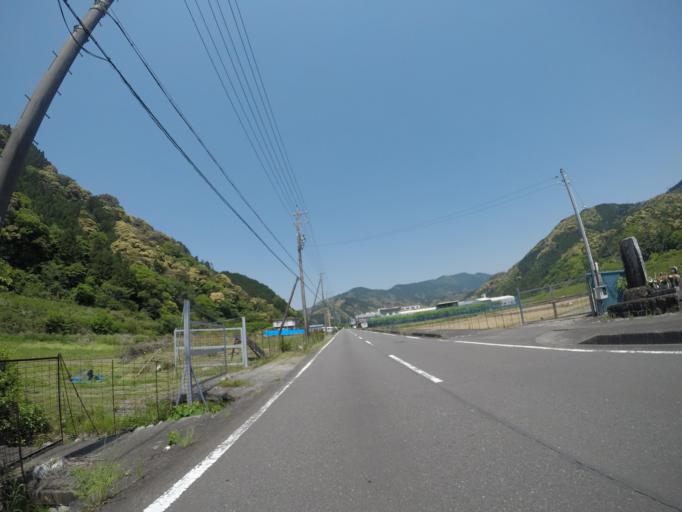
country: JP
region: Shizuoka
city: Shizuoka-shi
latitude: 34.9989
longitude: 138.2843
